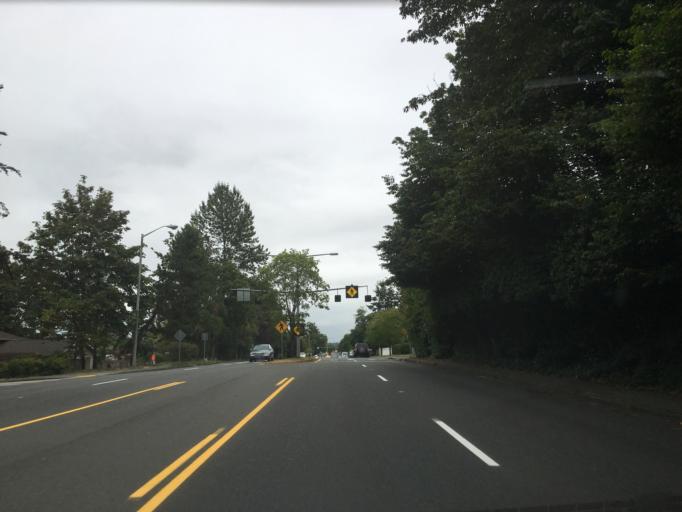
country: US
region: Washington
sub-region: King County
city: Kingsgate
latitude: 47.7112
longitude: -122.2017
